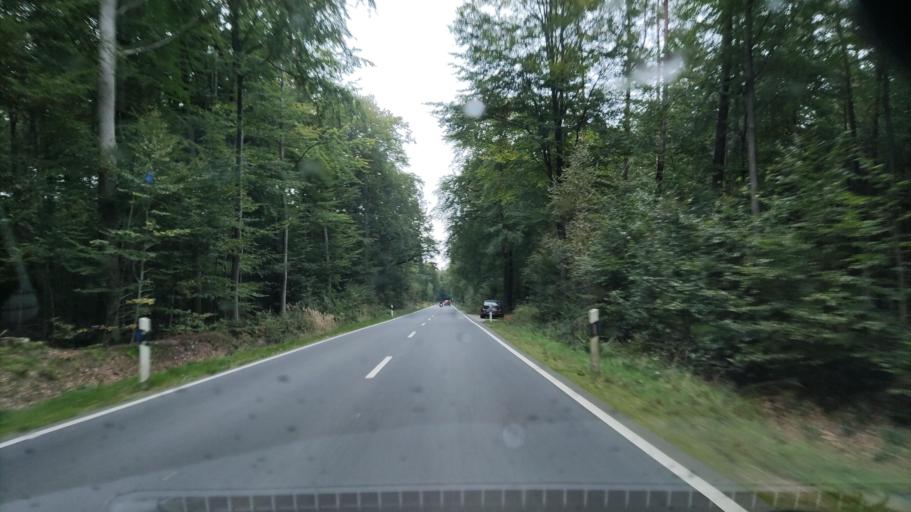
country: DE
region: Schleswig-Holstein
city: Witzhave
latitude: 53.5473
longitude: 10.3508
